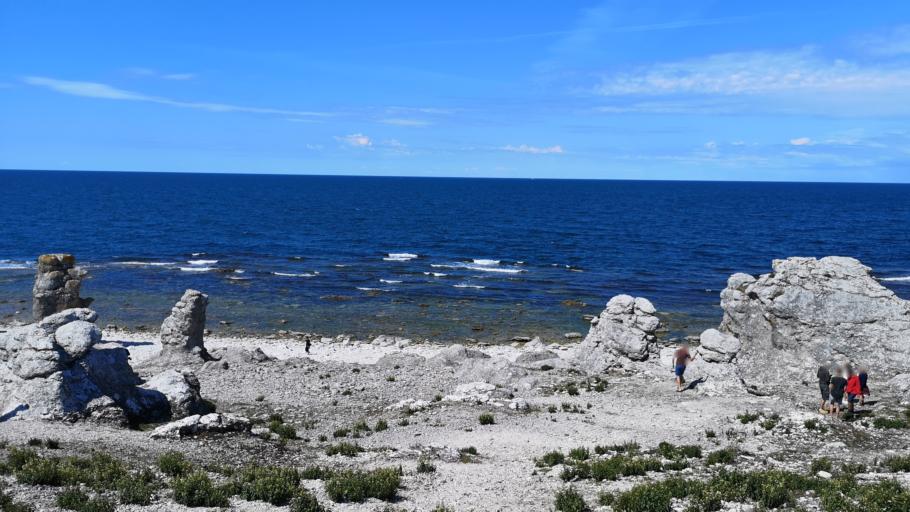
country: SE
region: Gotland
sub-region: Gotland
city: Slite
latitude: 57.9974
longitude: 19.1815
